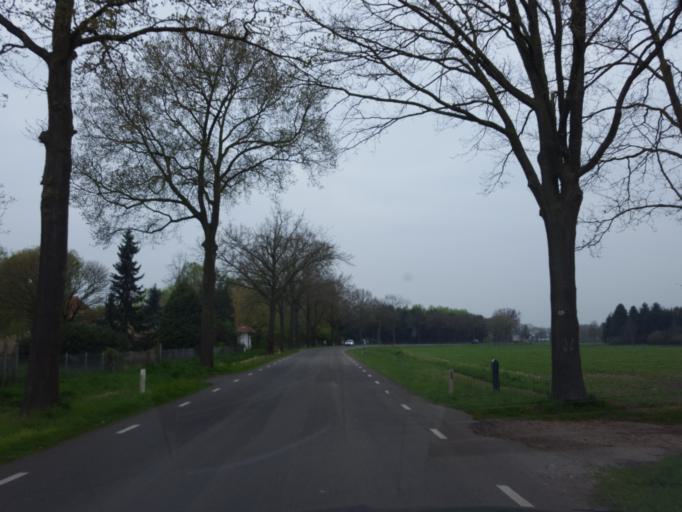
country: NL
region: Limburg
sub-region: Gemeente Nederweert
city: Nederweert
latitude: 51.3143
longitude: 5.7071
